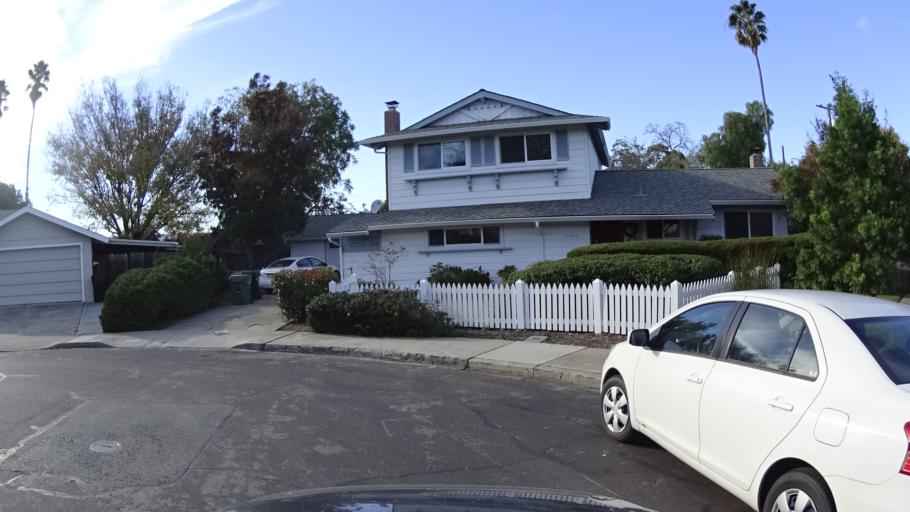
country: US
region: California
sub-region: Santa Clara County
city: Santa Clara
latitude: 37.3566
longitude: -121.9767
